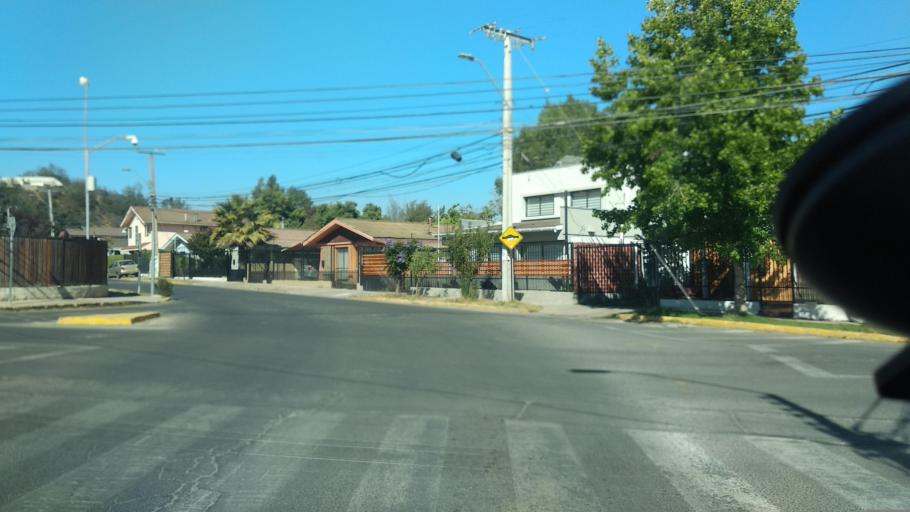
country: CL
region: Valparaiso
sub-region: Provincia de Marga Marga
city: Villa Alemana
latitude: -33.0388
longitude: -71.3879
